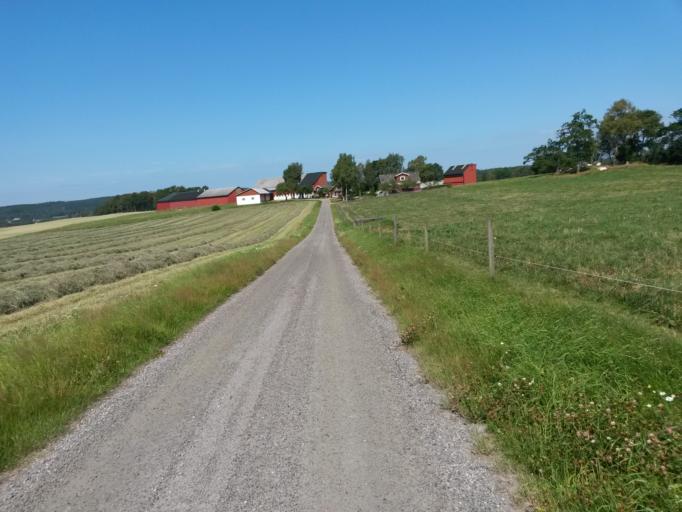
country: SE
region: Vaestra Goetaland
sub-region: Vargarda Kommun
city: Jonstorp
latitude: 57.9804
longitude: 12.6490
